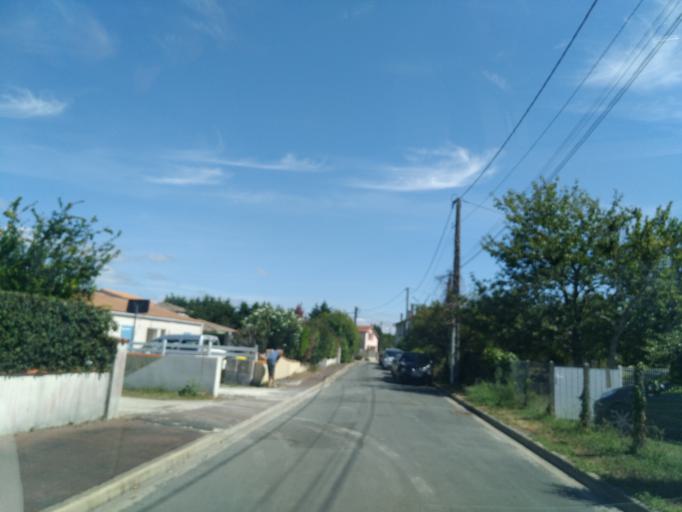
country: FR
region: Poitou-Charentes
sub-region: Departement de la Charente-Maritime
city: Saint-Palais-sur-Mer
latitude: 45.6577
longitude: -1.0780
